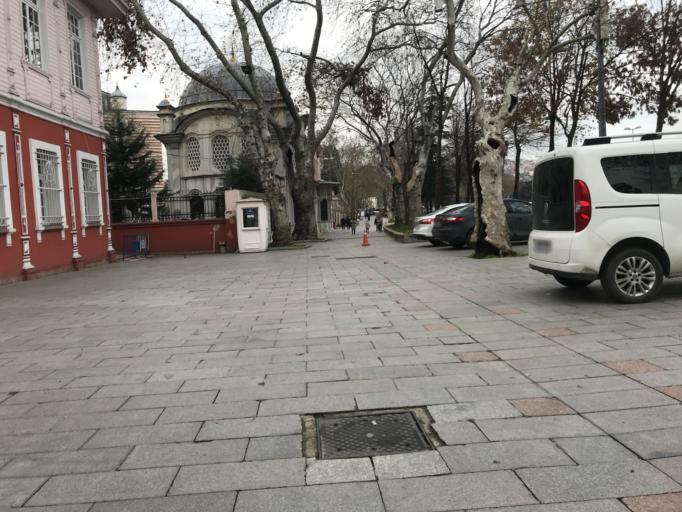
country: TR
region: Istanbul
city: Istanbul
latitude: 41.0438
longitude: 28.9367
